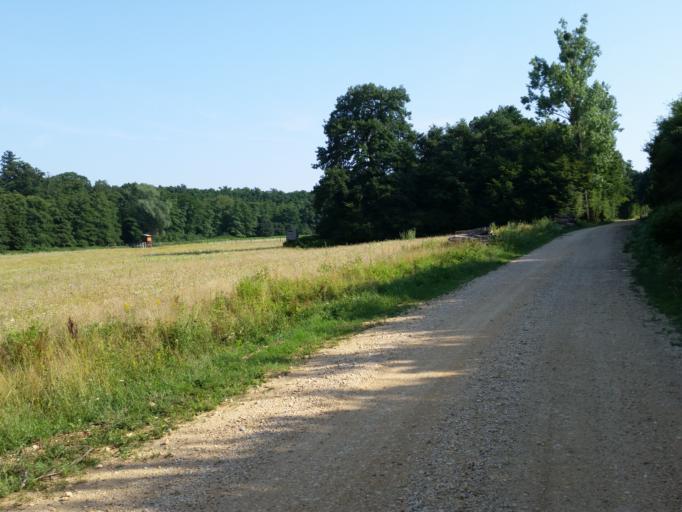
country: HU
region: Vas
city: Sarvar
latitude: 47.1476
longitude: 16.9684
